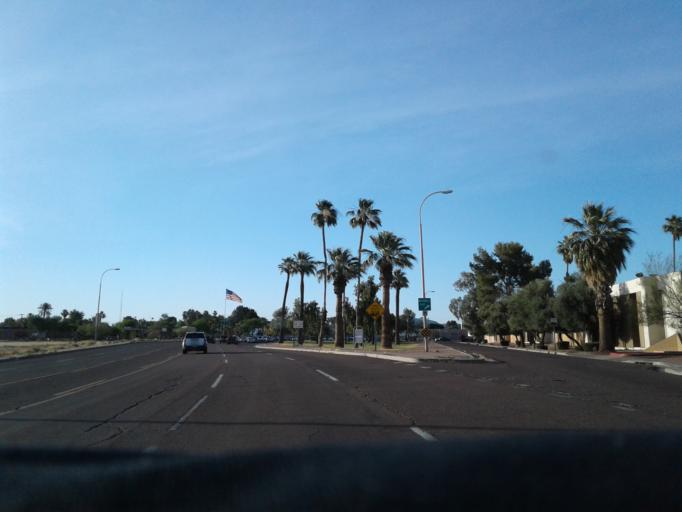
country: US
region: Arizona
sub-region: Maricopa County
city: Tempe Junction
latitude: 33.4634
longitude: -111.9950
